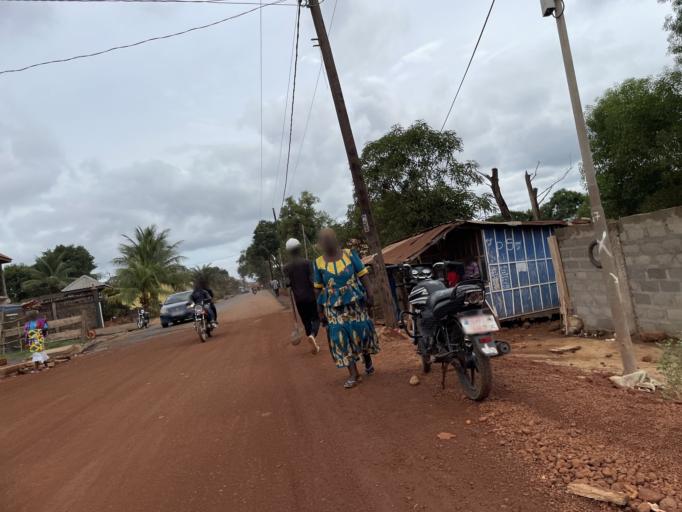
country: SL
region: Western Area
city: Hastings
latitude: 8.4029
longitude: -13.1441
